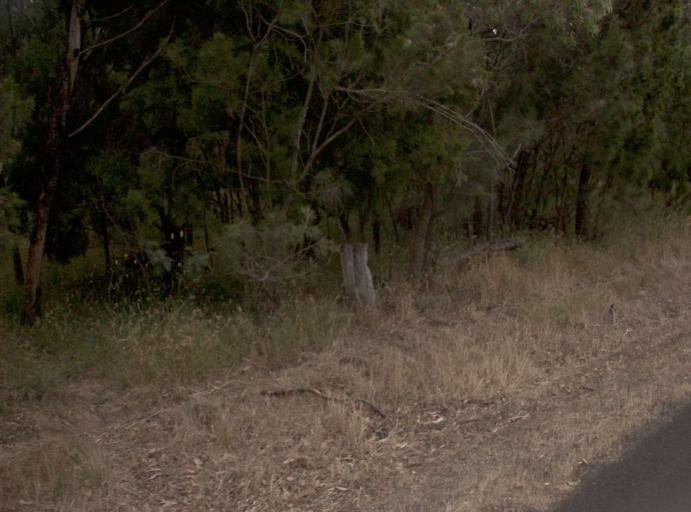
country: AU
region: Victoria
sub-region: Wellington
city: Sale
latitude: -38.4146
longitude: 146.9614
